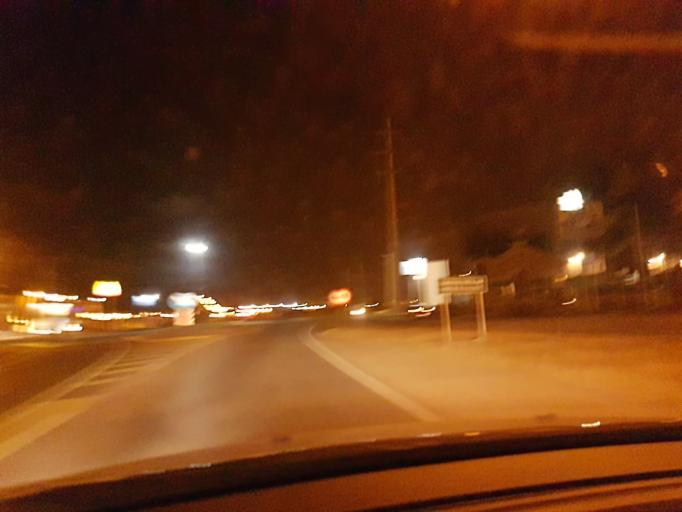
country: AR
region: Cordoba
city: Villa Allende
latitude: -31.3006
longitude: -64.2787
